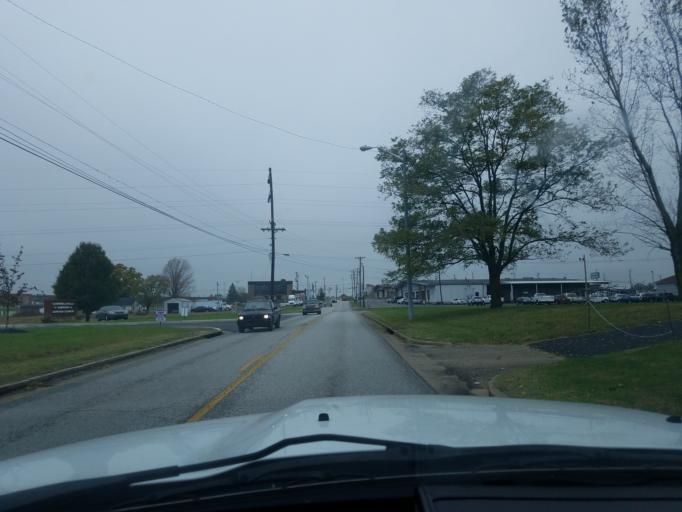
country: US
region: Kentucky
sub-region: Taylor County
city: Campbellsville
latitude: 37.3493
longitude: -85.3301
